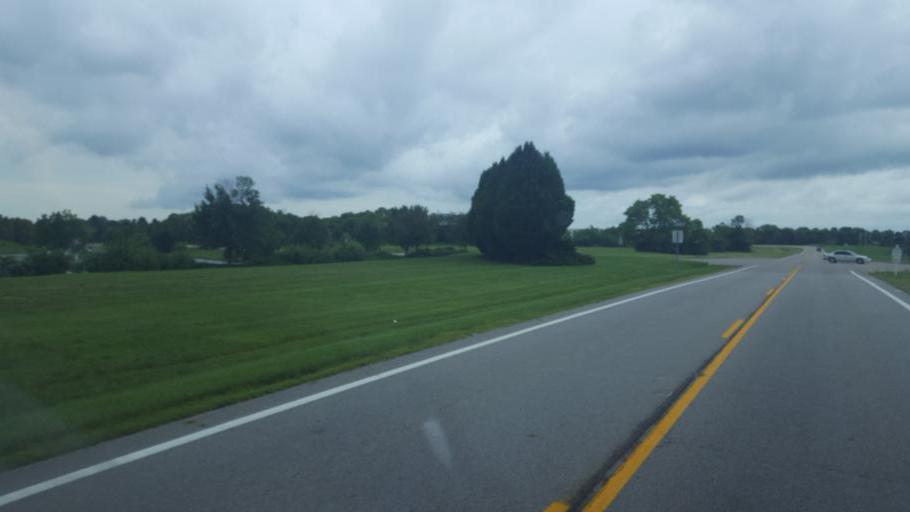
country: US
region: Ohio
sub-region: Franklin County
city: Groveport
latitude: 39.8427
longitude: -82.9061
